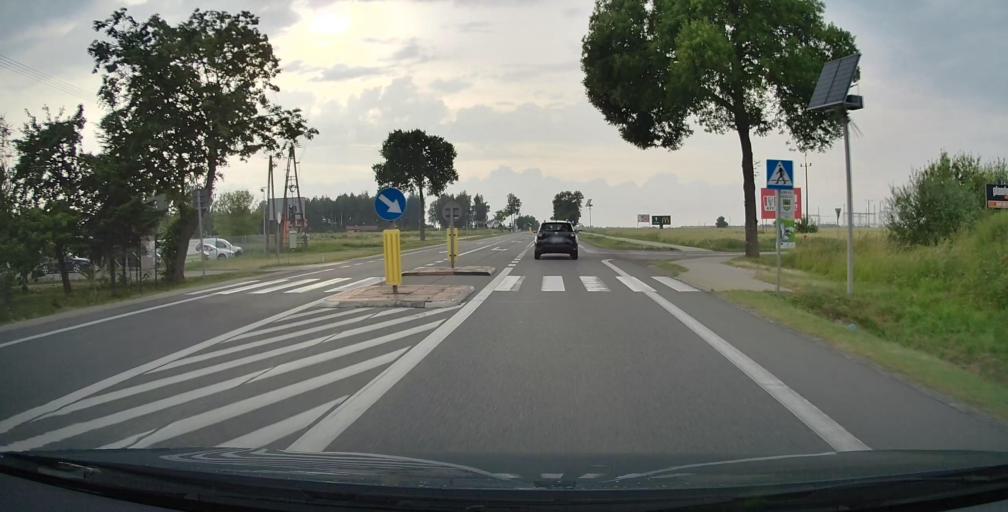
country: PL
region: Masovian Voivodeship
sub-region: Siedlce
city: Siedlce
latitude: 52.1243
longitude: 22.3480
